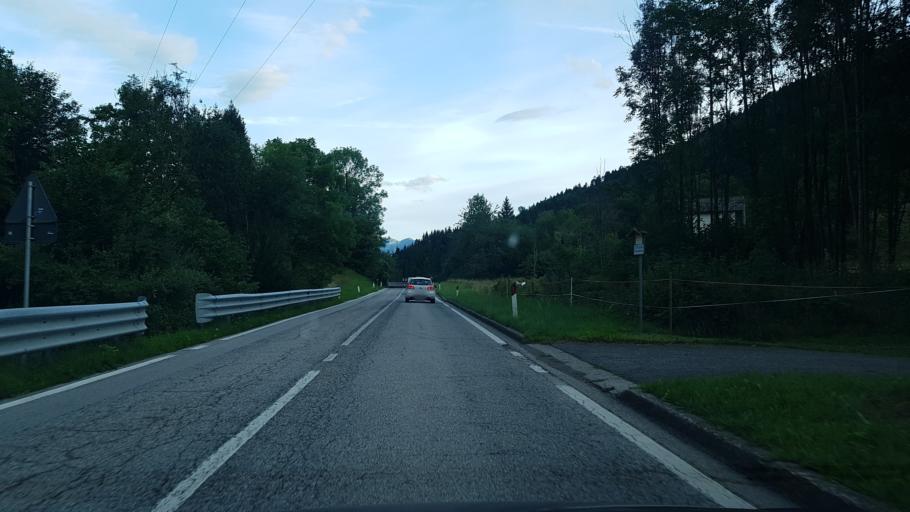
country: IT
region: Friuli Venezia Giulia
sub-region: Provincia di Udine
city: Comeglians
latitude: 46.5395
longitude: 12.8648
